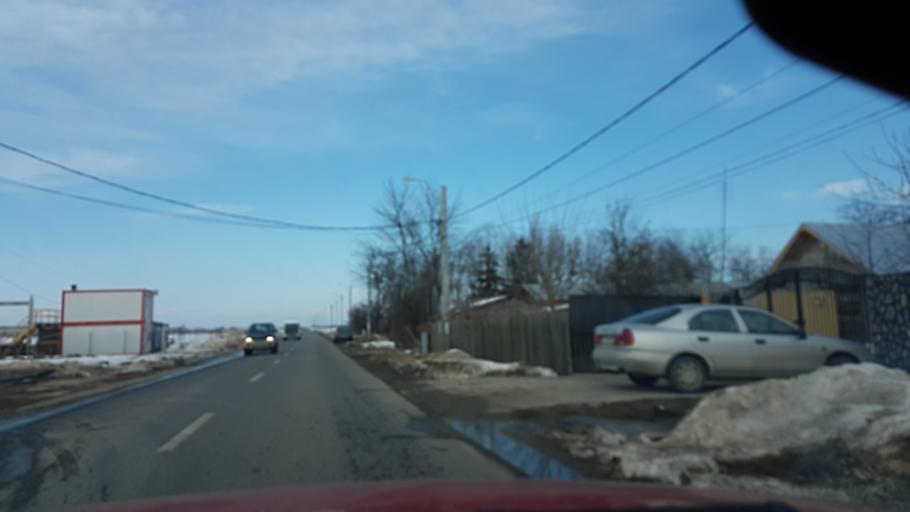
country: RO
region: Ilfov
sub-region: Comuna Tunari
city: Tunari
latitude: 44.5584
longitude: 26.1427
